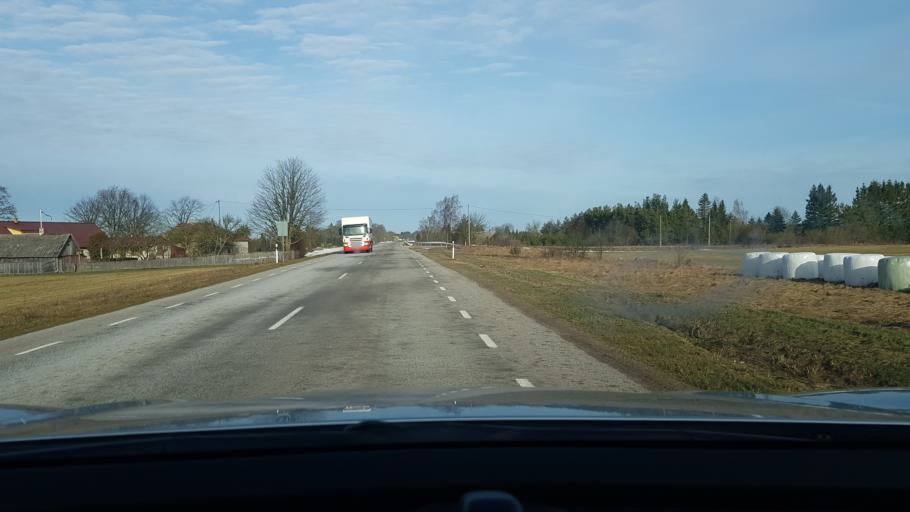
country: EE
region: Saare
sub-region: Kuressaare linn
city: Kuressaare
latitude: 58.5166
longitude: 22.7038
